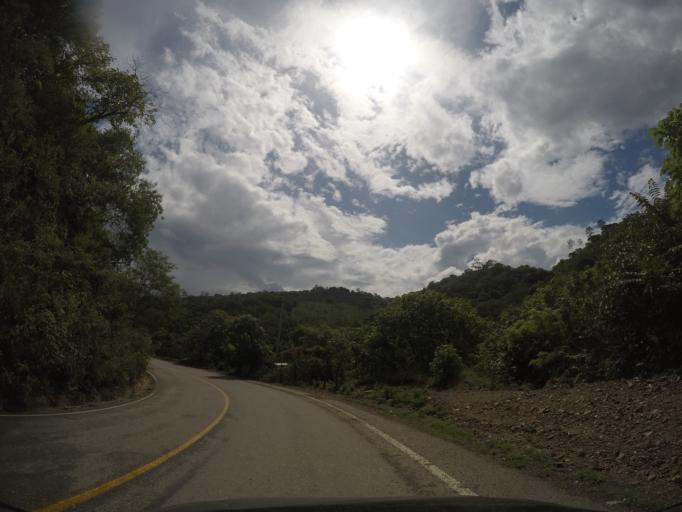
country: MX
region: Oaxaca
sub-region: San Jeronimo Coatlan
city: San Cristobal Honduras
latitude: 16.3774
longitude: -97.0779
